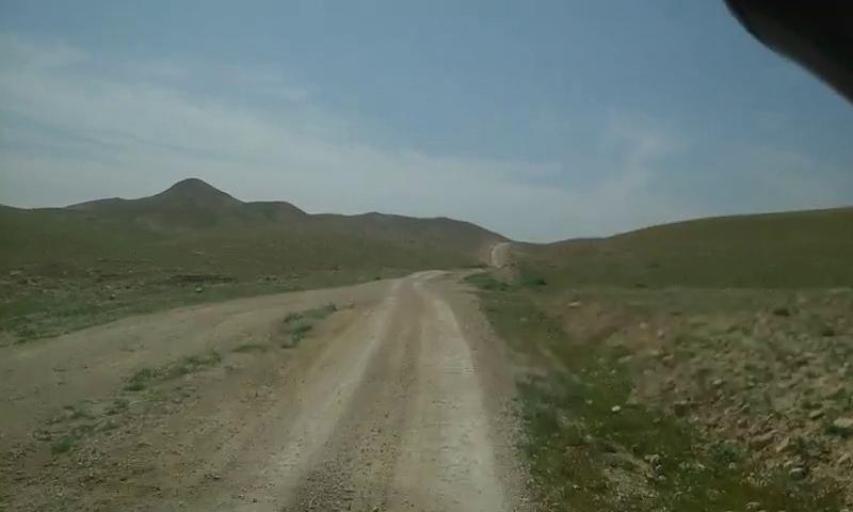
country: PS
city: `Arab ar Rashaydah
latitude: 31.4884
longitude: 35.2842
